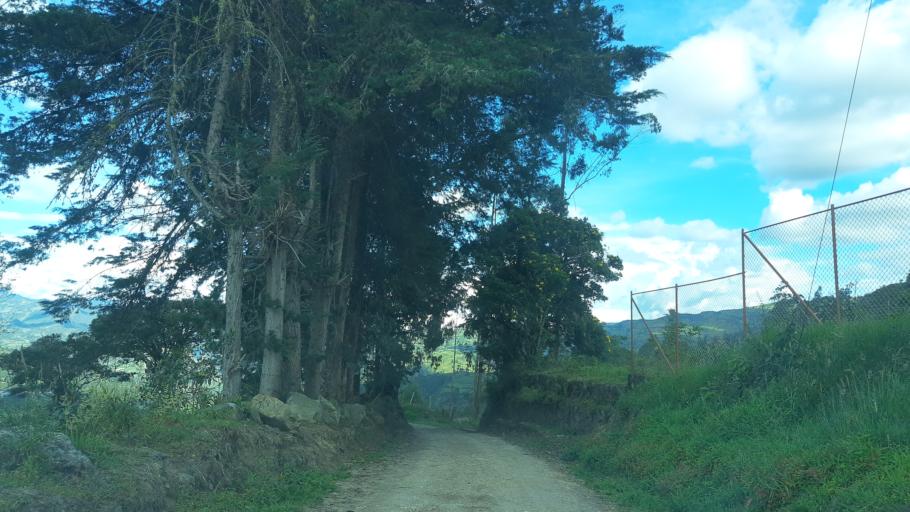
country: CO
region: Cundinamarca
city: Macheta
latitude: 5.0706
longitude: -73.6306
